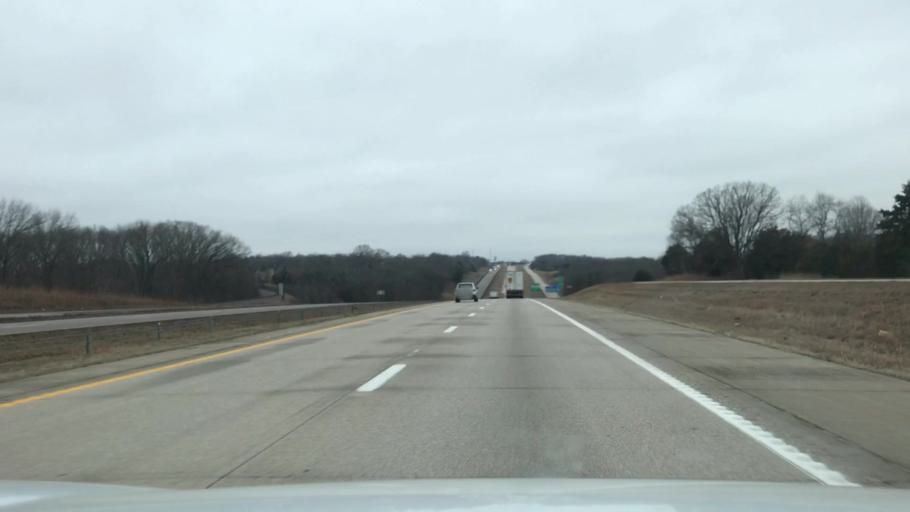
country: US
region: Missouri
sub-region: Crawford County
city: Bourbon
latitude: 38.1636
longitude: -91.2261
